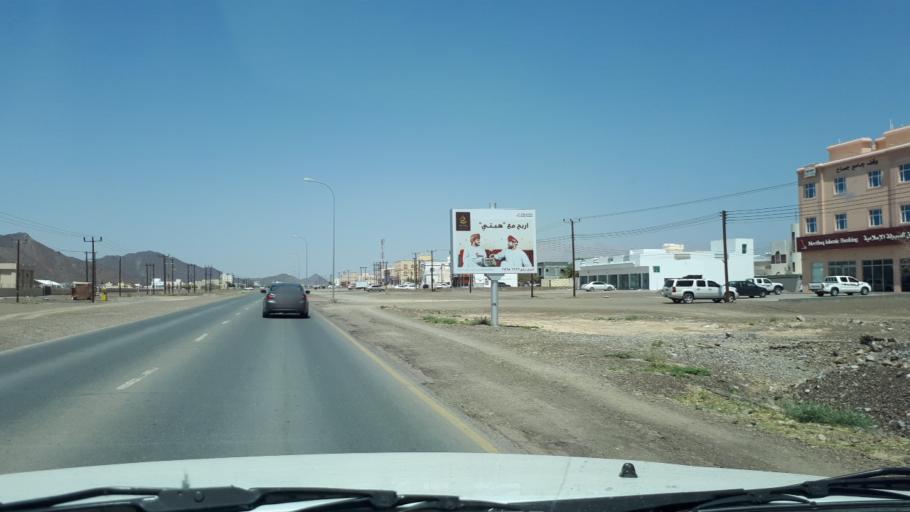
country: OM
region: Muhafazat ad Dakhiliyah
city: Bahla'
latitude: 22.9474
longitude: 57.2677
